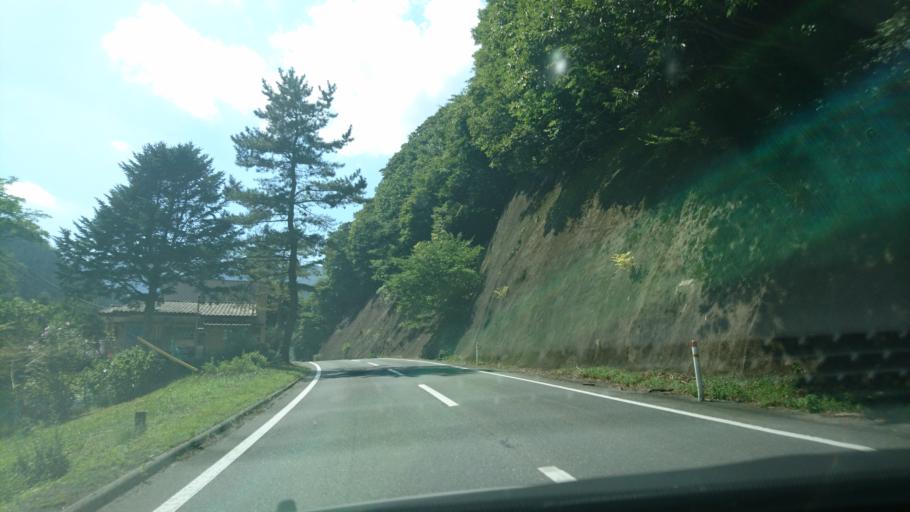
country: JP
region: Iwate
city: Ofunato
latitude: 39.0274
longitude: 141.5112
